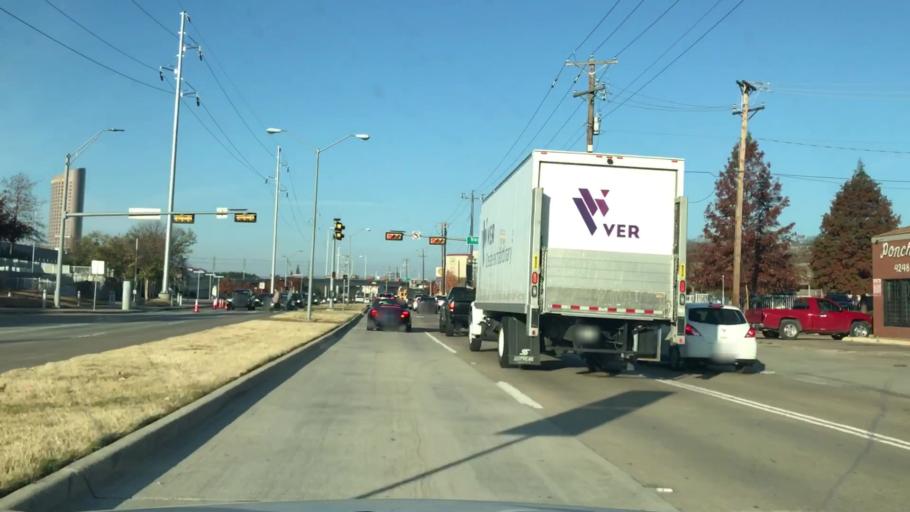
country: US
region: Texas
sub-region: Dallas County
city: Dallas
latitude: 32.8049
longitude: -96.8234
